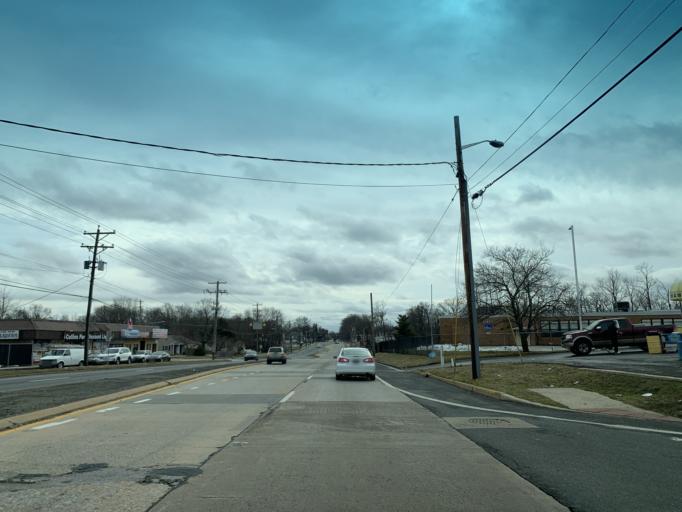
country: US
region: Delaware
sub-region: New Castle County
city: New Castle
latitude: 39.6871
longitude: -75.5569
